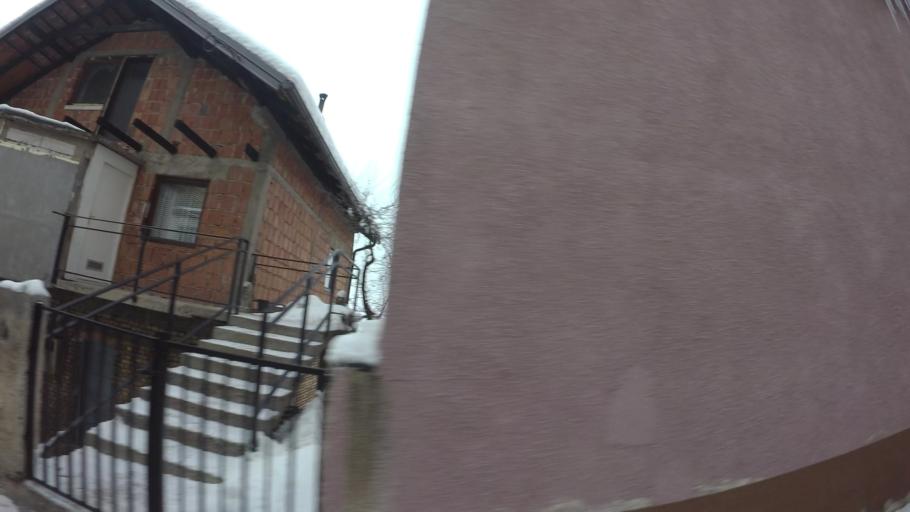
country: BA
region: Federation of Bosnia and Herzegovina
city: Kobilja Glava
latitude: 43.8694
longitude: 18.4375
